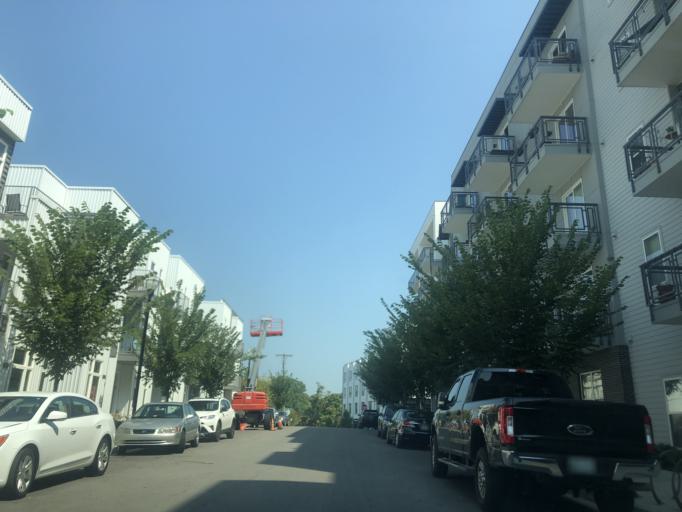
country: US
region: Tennessee
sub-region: Davidson County
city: Nashville
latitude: 36.1830
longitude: -86.7505
